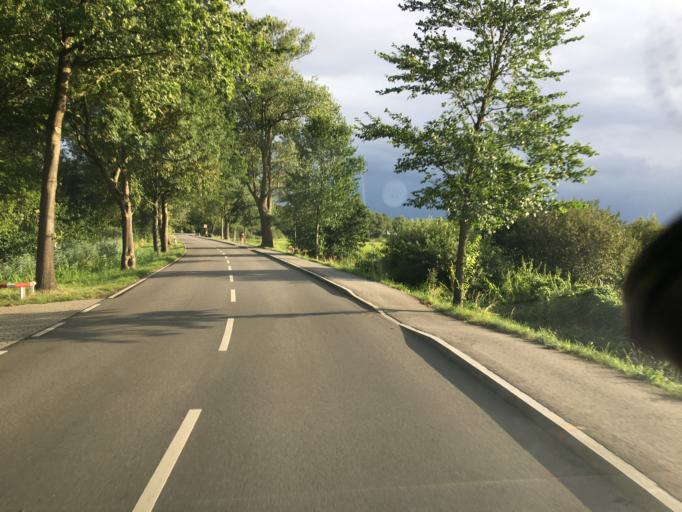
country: DE
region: Lower Saxony
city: Neu Wulmstorf
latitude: 53.4886
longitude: 9.8680
